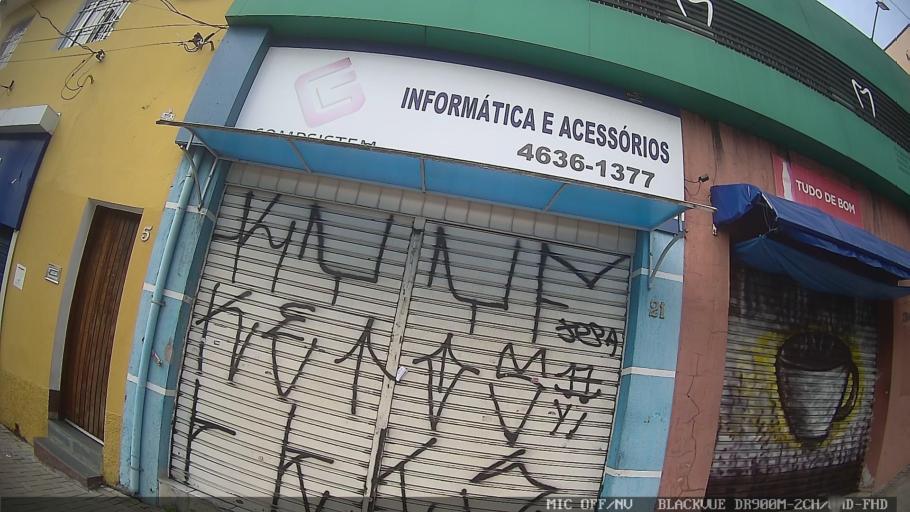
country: BR
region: Sao Paulo
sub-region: Poa
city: Poa
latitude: -23.5203
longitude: -46.3433
